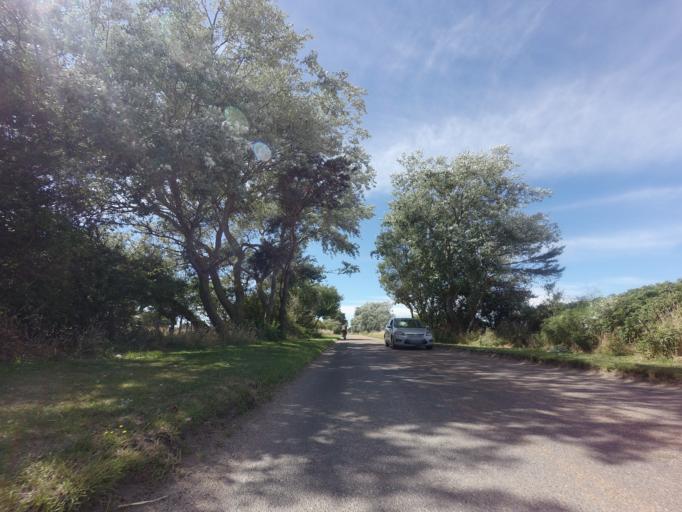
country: GB
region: England
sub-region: Kent
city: Sandwich
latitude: 51.2690
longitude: 1.3733
